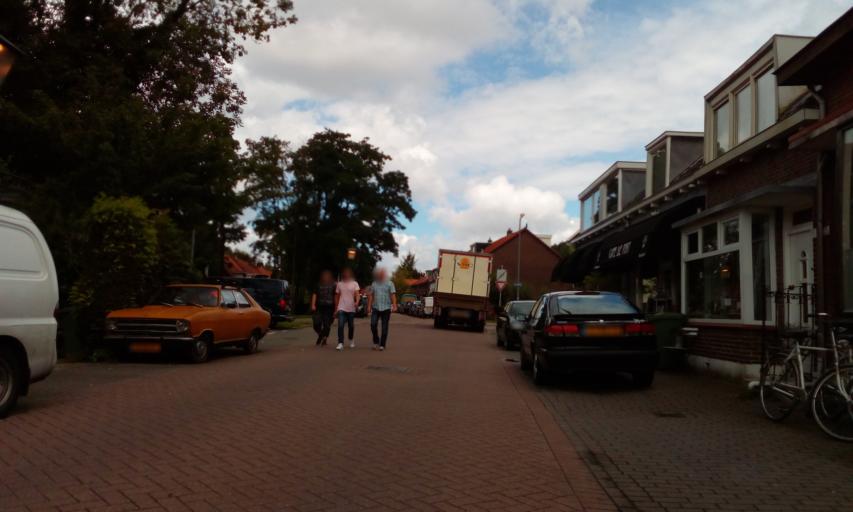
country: NL
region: South Holland
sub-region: Gemeente Barendrecht
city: Barendrecht
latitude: 51.8743
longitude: 4.5431
